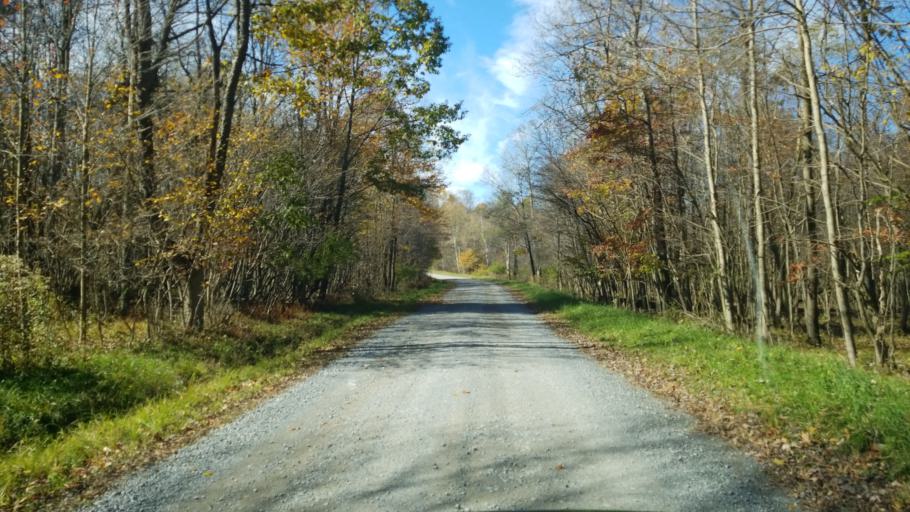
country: US
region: Pennsylvania
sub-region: Jefferson County
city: Falls Creek
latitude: 41.1915
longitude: -78.7818
